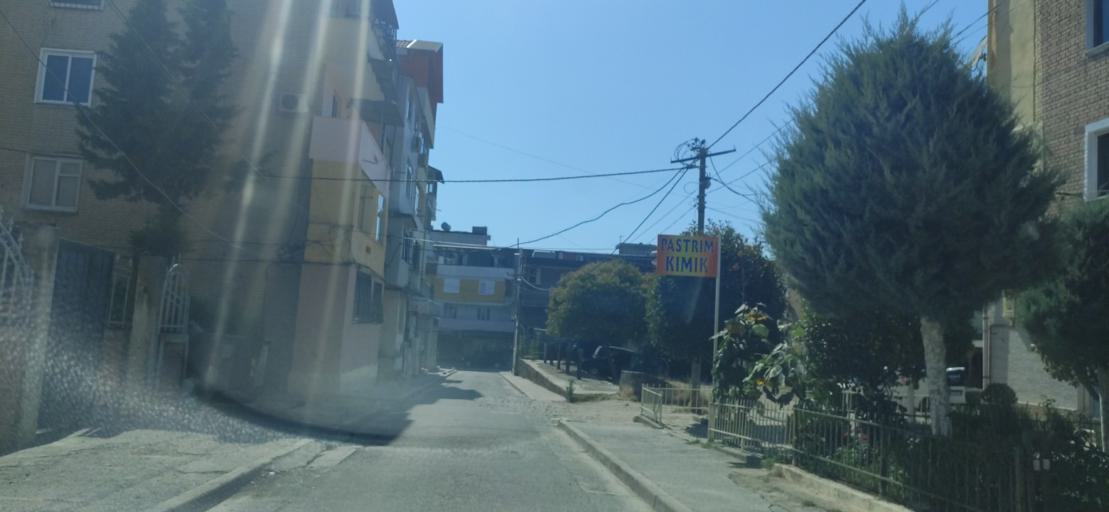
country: AL
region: Lezhe
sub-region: Rrethi i Kurbinit
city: Lac
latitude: 41.6368
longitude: 19.7140
